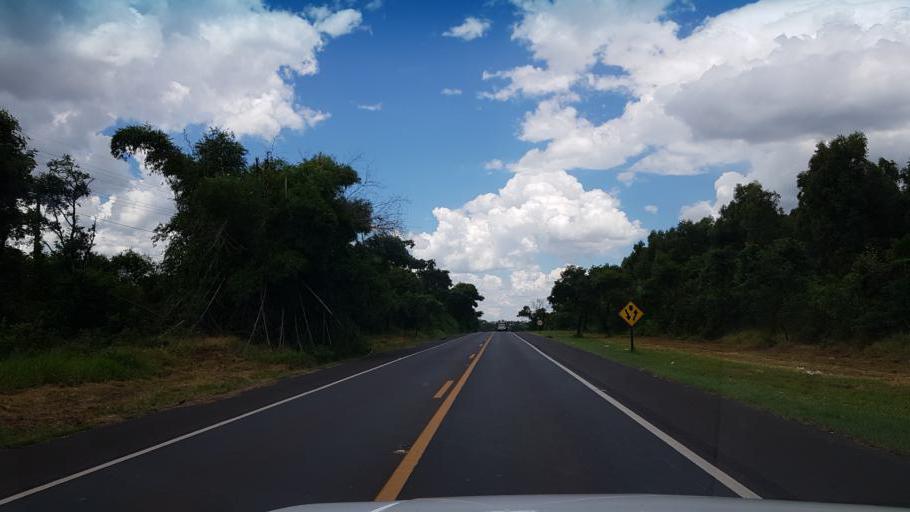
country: BR
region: Sao Paulo
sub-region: Paraguacu Paulista
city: Paraguacu Paulista
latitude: -22.4044
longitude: -50.6015
